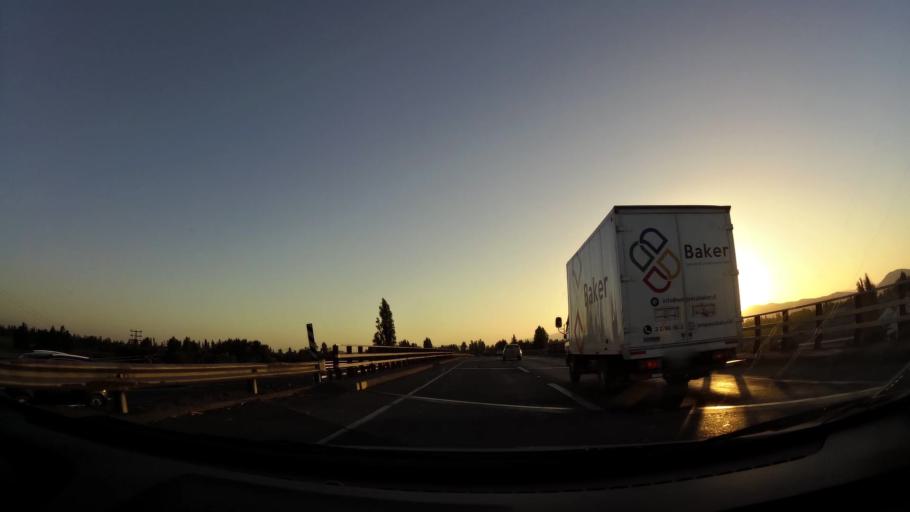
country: CL
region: Maule
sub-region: Provincia de Linares
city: San Javier
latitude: -35.5742
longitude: -71.7019
